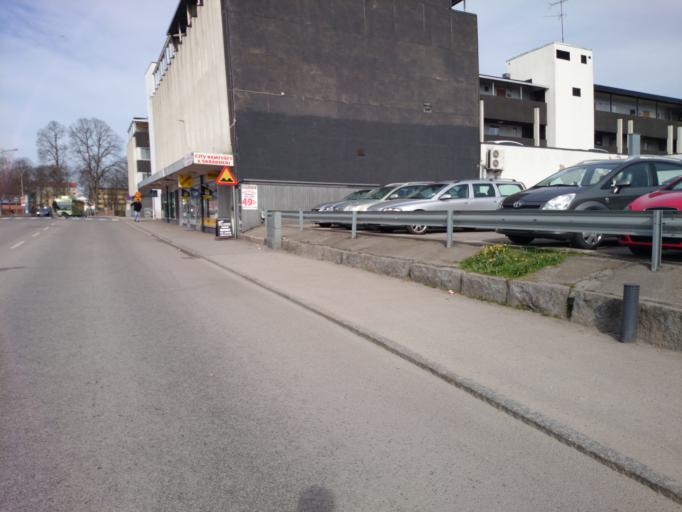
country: SE
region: Kronoberg
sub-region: Vaxjo Kommun
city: Vaexjoe
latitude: 56.8773
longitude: 14.8059
